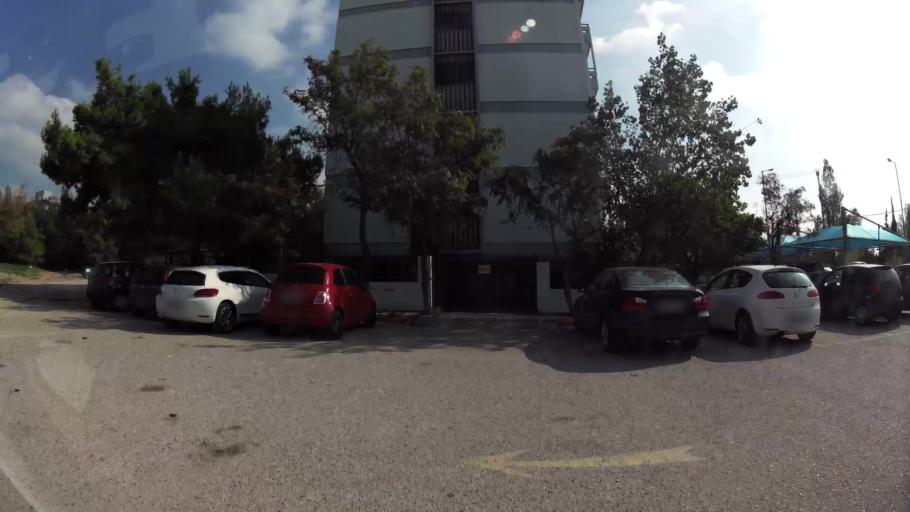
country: GR
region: Attica
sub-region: Nomarchia Athinas
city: Papagou
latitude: 37.9837
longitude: 23.7837
